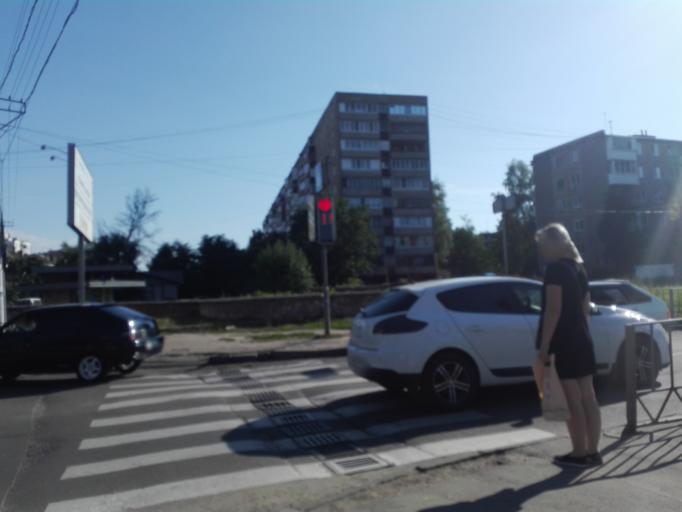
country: RU
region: Orjol
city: Orel
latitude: 52.9814
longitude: 36.0697
